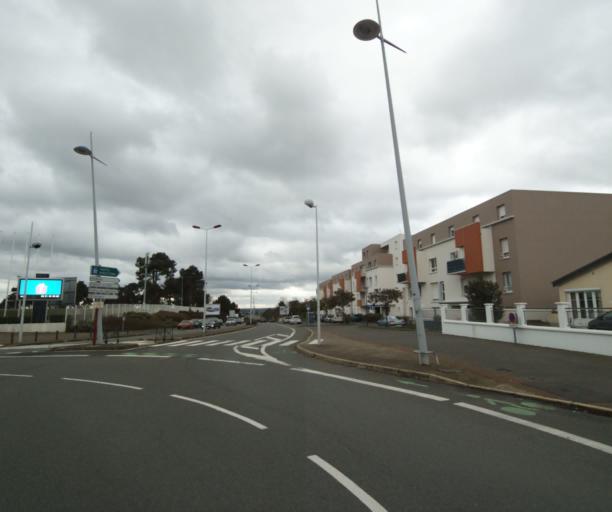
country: FR
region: Pays de la Loire
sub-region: Departement de la Sarthe
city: Arnage
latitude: 47.9603
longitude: 0.1998
